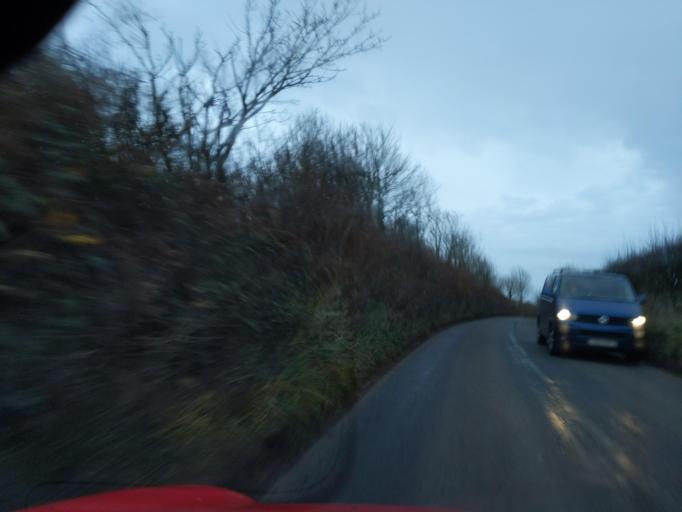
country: GB
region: England
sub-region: Devon
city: Wembury
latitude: 50.3351
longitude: -4.0696
